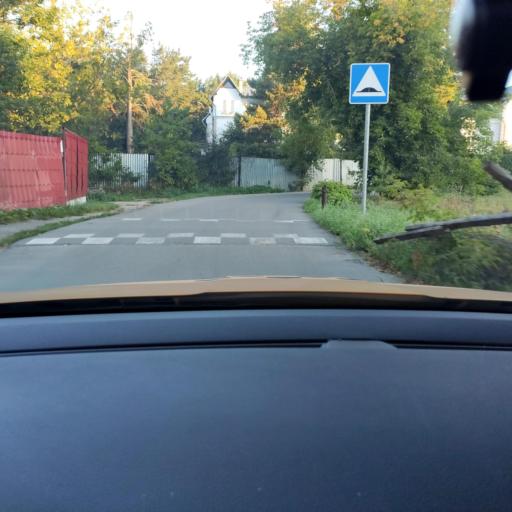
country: RU
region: Moskovskaya
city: Oktyabr'skiy
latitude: 55.6146
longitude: 37.9651
